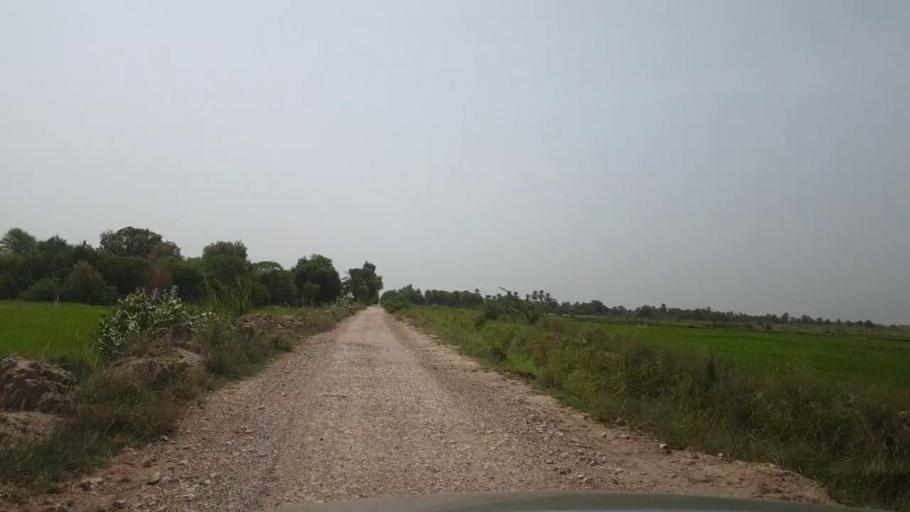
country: PK
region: Sindh
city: Madeji
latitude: 27.8289
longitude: 68.4308
